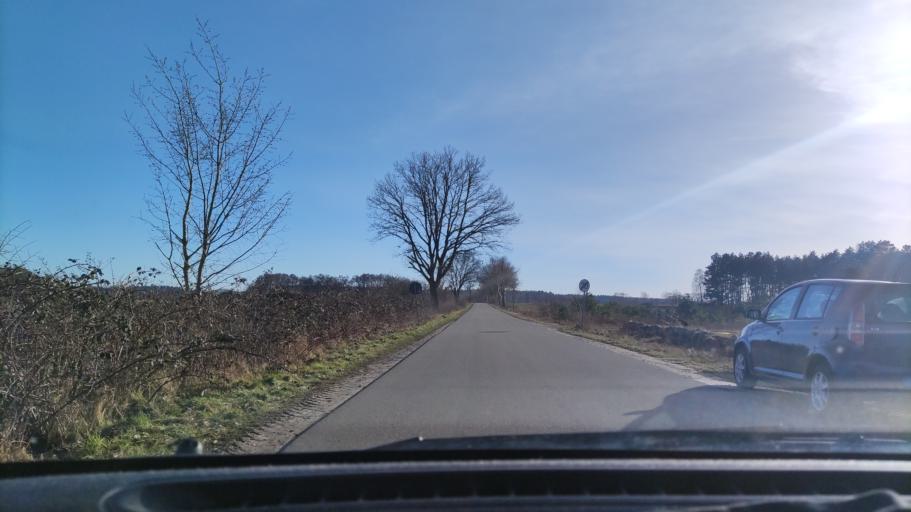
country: DE
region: Lower Saxony
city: Tosterglope
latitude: 53.1914
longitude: 10.8572
